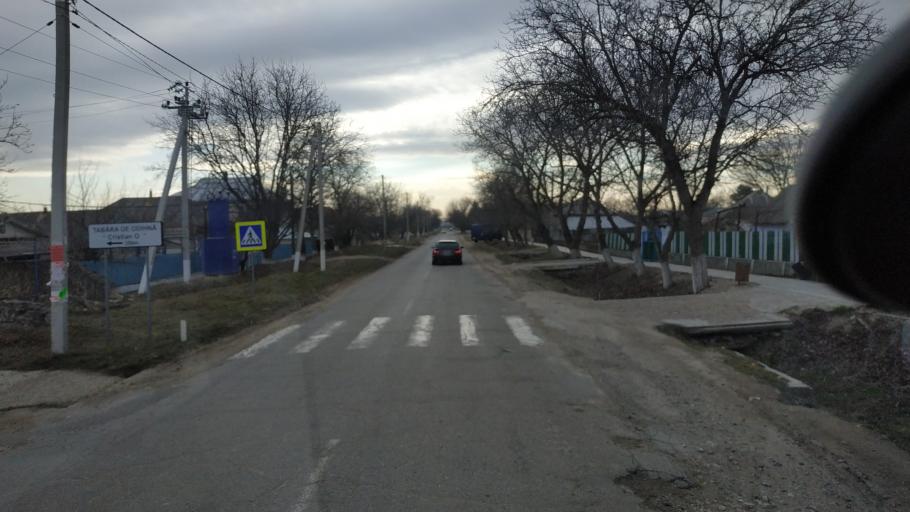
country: MD
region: Criuleni
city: Criuleni
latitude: 47.1689
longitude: 29.1253
